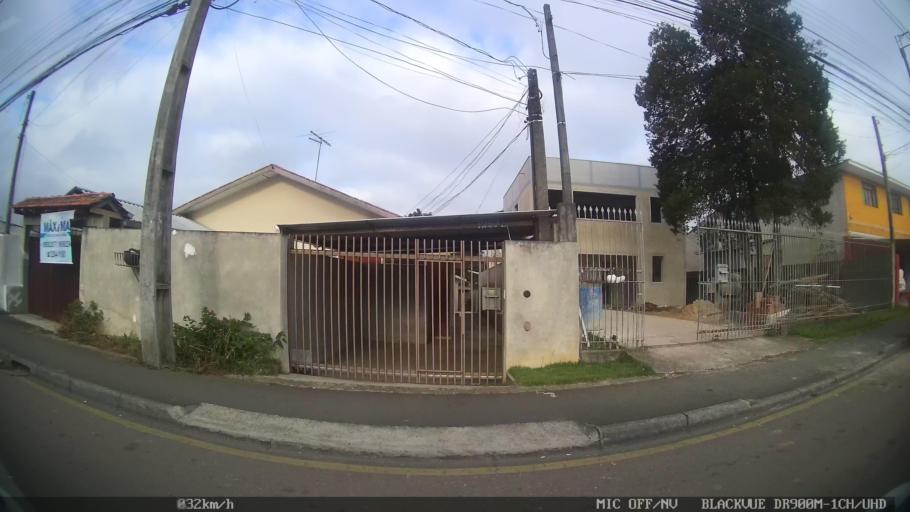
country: BR
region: Parana
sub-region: Curitiba
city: Curitiba
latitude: -25.4007
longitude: -49.3128
